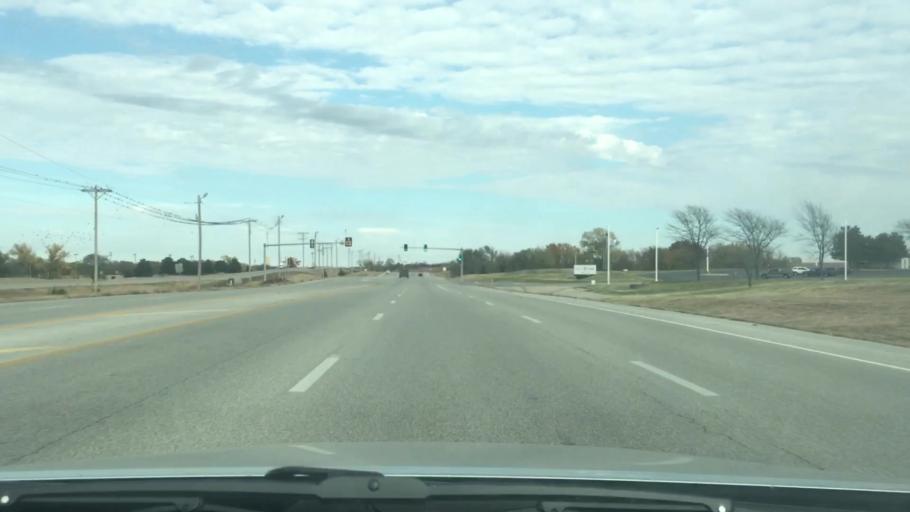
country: US
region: Kansas
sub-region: Sedgwick County
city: Wichita
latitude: 37.6511
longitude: -97.2687
